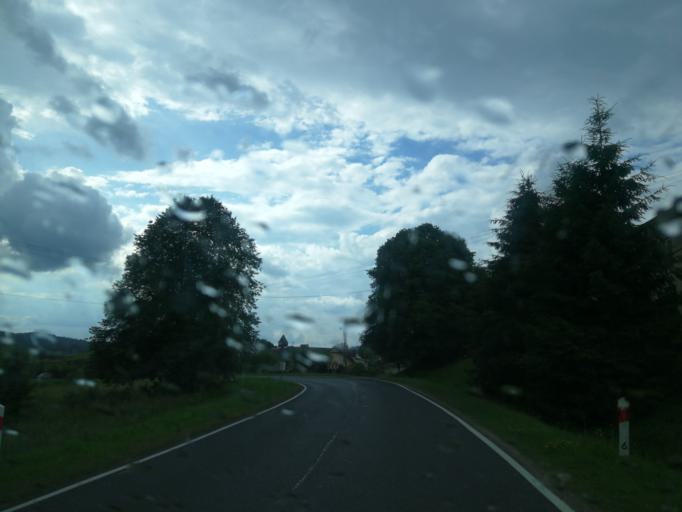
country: PL
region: Subcarpathian Voivodeship
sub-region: Powiat leski
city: Uherce Mineralne
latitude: 49.4575
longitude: 22.4150
